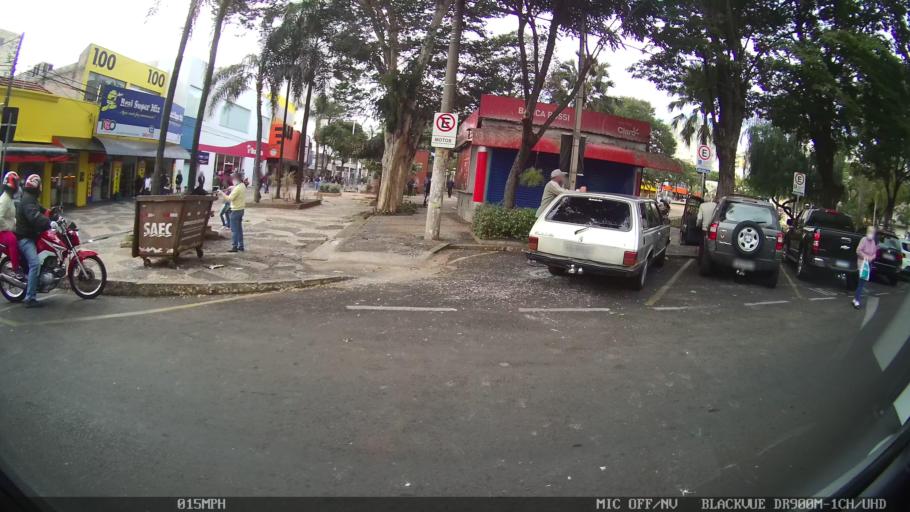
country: BR
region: Sao Paulo
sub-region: Catanduva
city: Catanduva
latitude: -21.1350
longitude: -48.9730
